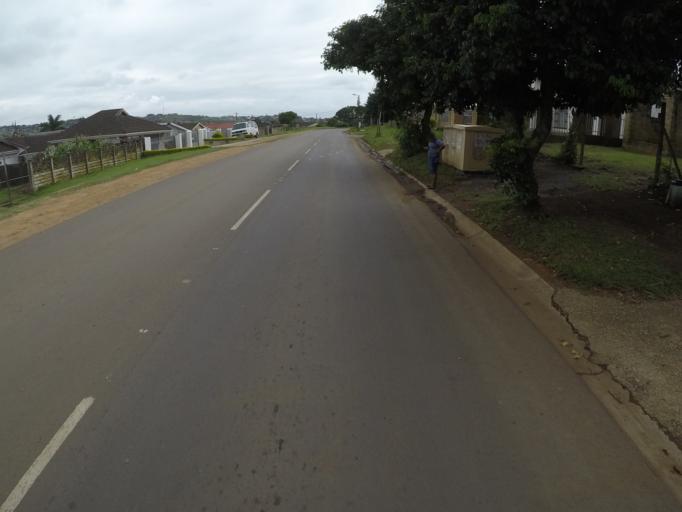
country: ZA
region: KwaZulu-Natal
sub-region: uThungulu District Municipality
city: Empangeni
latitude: -28.7842
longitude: 31.8539
